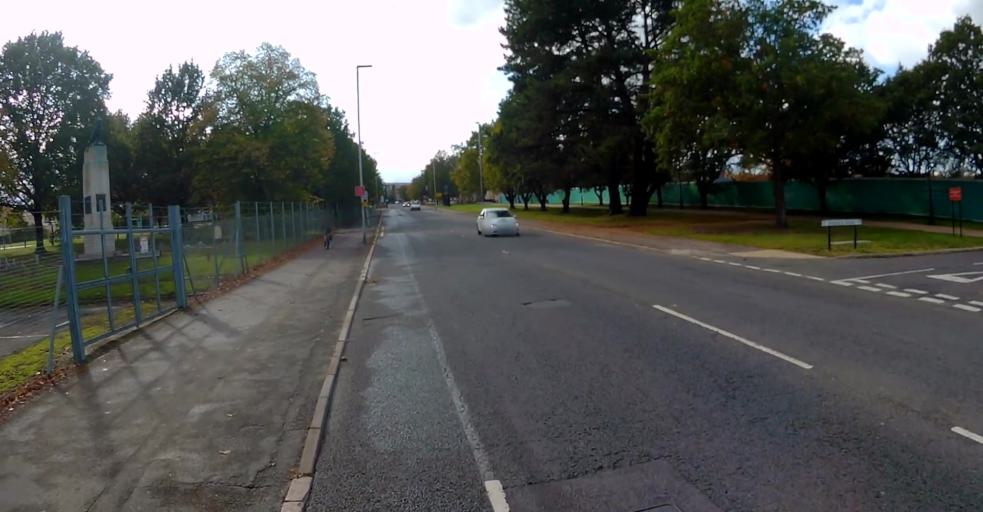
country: GB
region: England
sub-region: Hampshire
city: Aldershot
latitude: 51.2583
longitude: -0.7621
